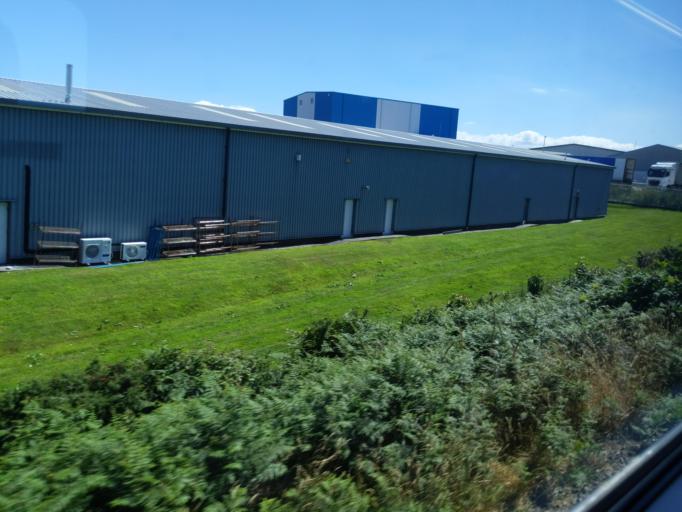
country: GB
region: England
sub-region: Cornwall
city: Redruth
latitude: 50.2449
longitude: -5.2228
